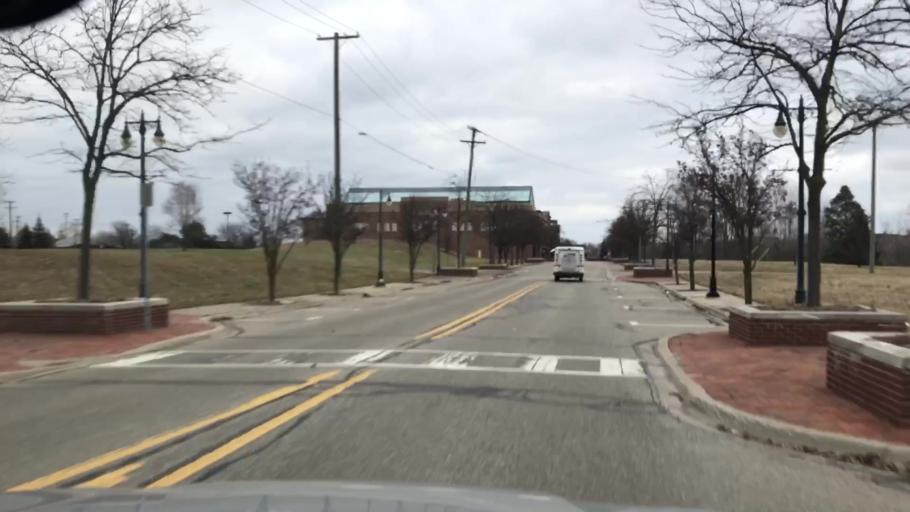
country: US
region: Michigan
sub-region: Oakland County
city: Novi
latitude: 42.4784
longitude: -83.4740
